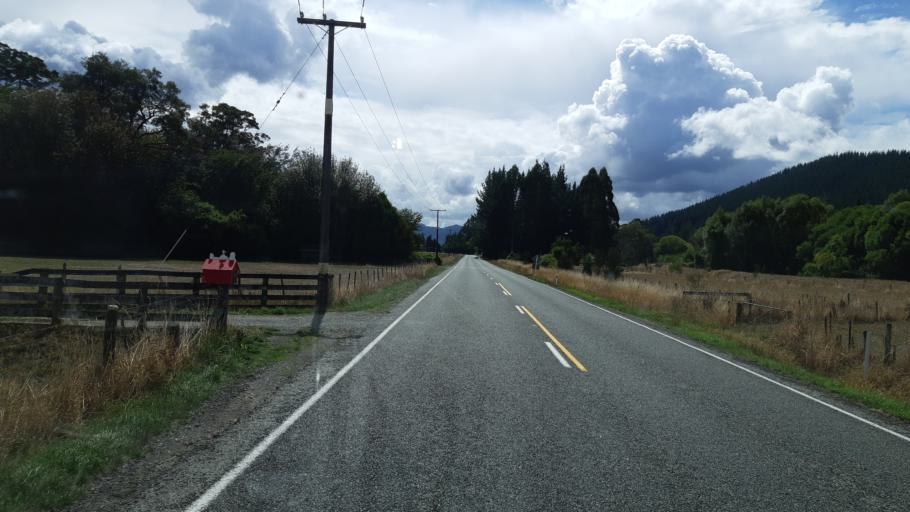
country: NZ
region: Tasman
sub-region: Tasman District
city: Wakefield
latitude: -41.4785
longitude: 172.8026
